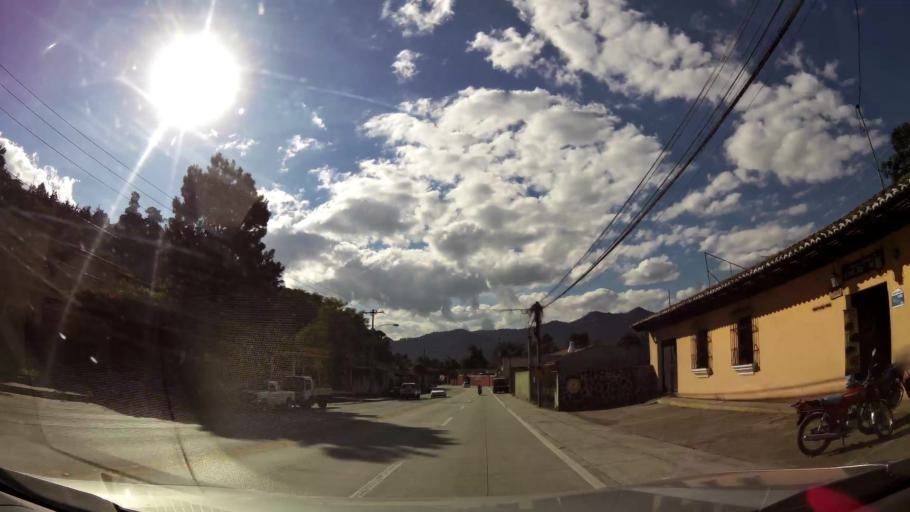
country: GT
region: Sacatepequez
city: Antigua Guatemala
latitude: 14.5590
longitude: -90.7232
